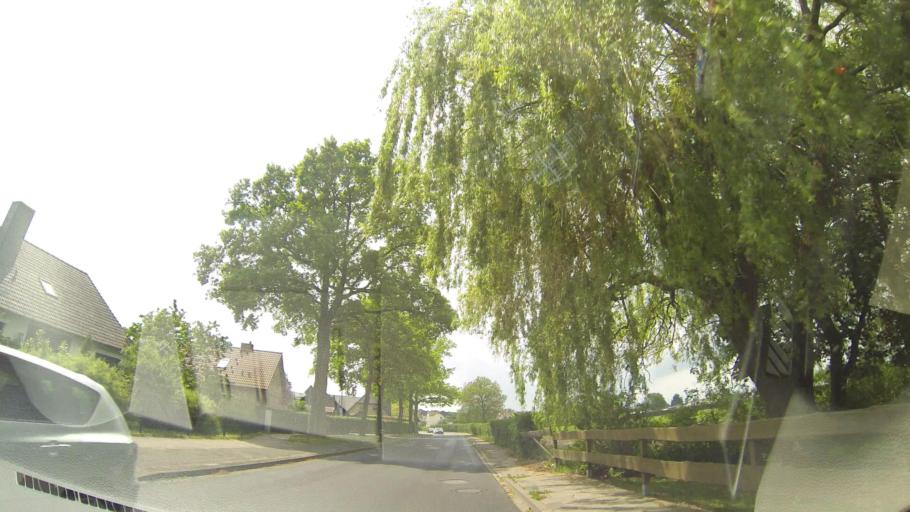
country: DE
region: Schleswig-Holstein
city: Tangstedt
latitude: 53.6591
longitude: 9.8416
